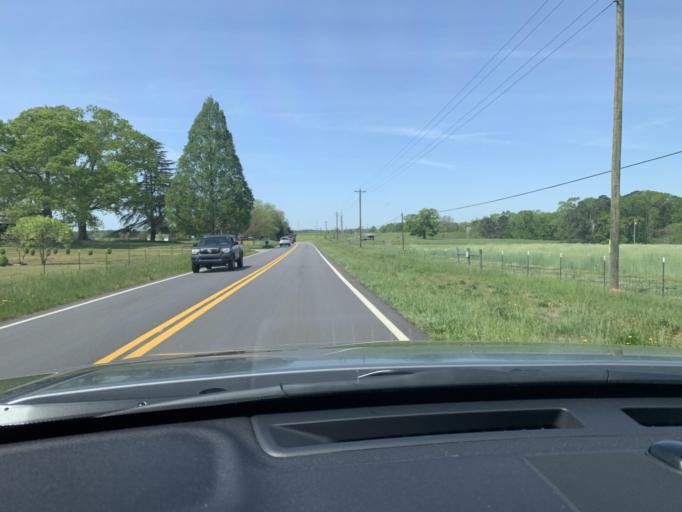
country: US
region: Georgia
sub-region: Oconee County
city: Watkinsville
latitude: 33.8876
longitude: -83.4196
